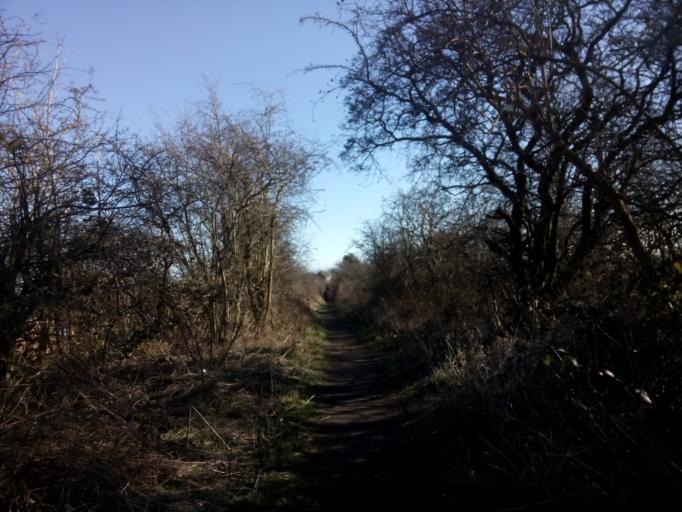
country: GB
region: England
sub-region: County Durham
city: Durham
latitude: 54.8001
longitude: -1.5886
